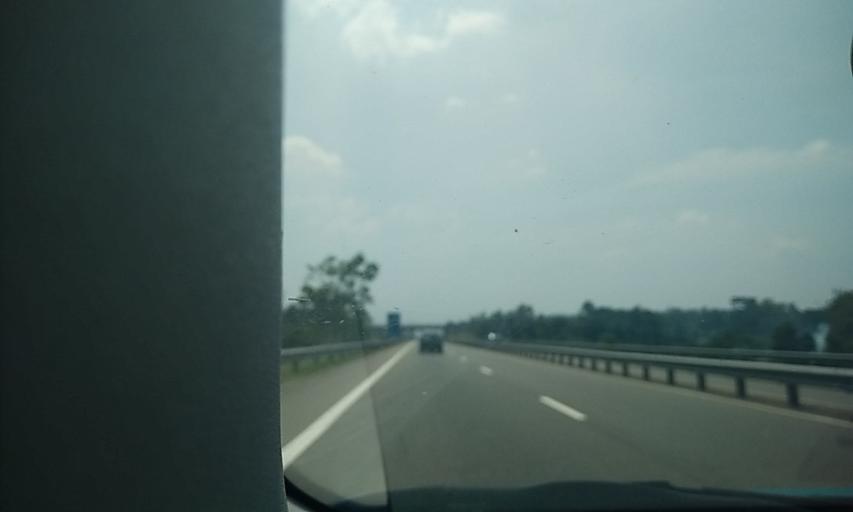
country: LK
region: Western
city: Horana South
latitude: 6.7269
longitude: 79.9992
